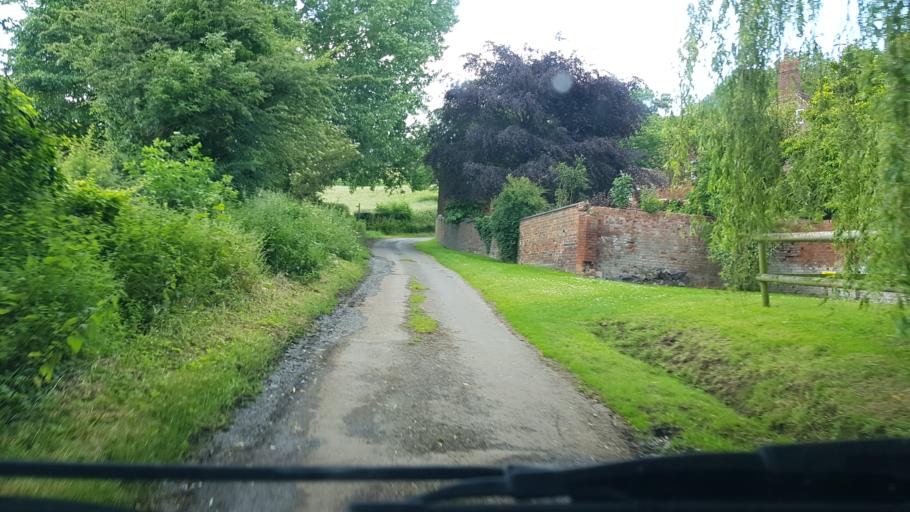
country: GB
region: England
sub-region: Shropshire
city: Romsley
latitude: 52.4625
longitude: -2.2649
